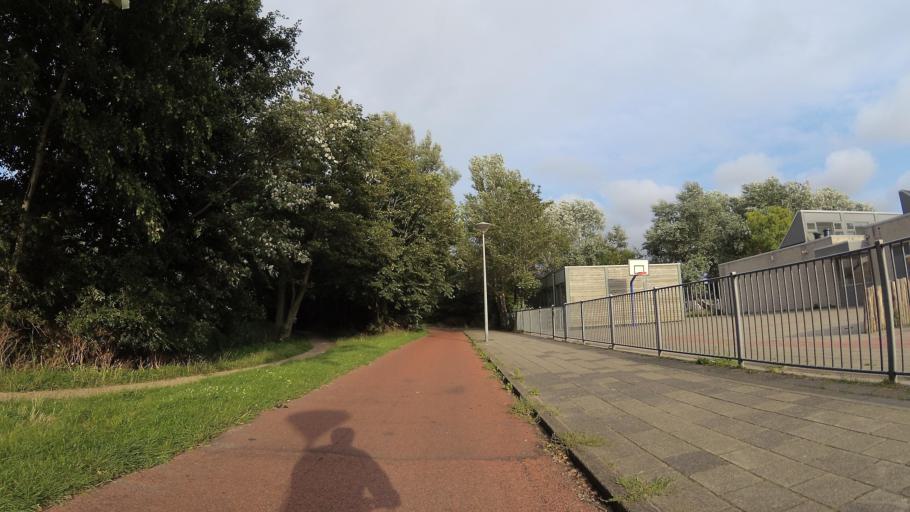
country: NL
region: North Holland
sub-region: Gemeente Den Helder
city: Den Helder
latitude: 52.8855
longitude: 4.7437
